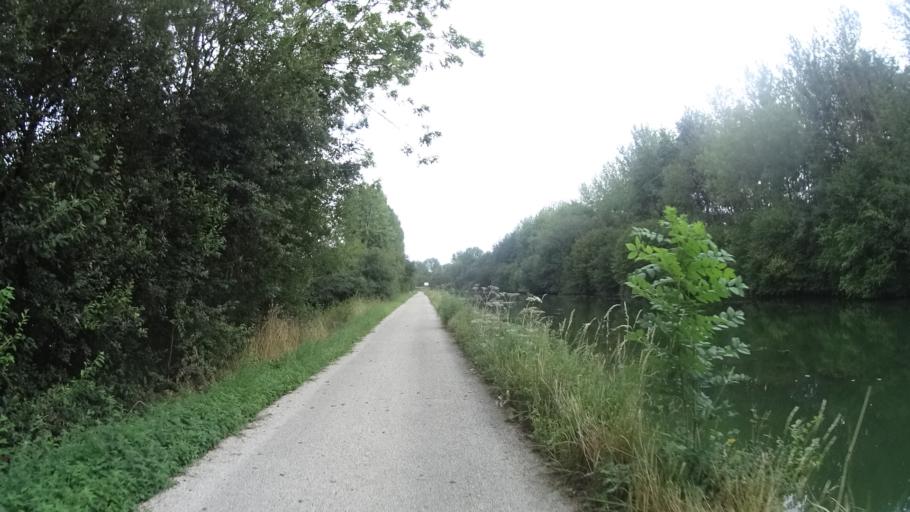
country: FR
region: Picardie
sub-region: Departement de l'Aisne
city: Ribemont
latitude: 49.7840
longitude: 3.4153
